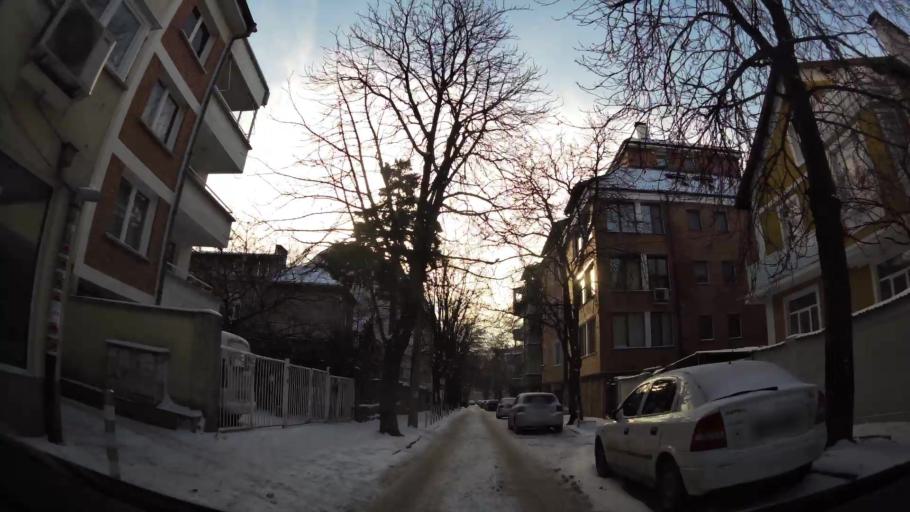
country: BG
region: Sofia-Capital
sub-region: Stolichna Obshtina
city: Sofia
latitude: 42.6735
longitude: 23.3341
